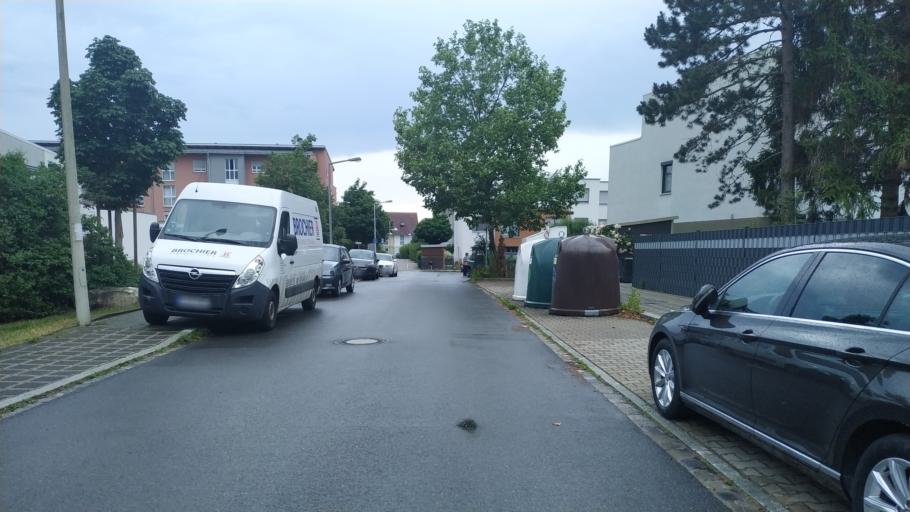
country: DE
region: Bavaria
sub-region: Regierungsbezirk Mittelfranken
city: Schwaig
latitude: 49.4646
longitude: 11.1464
